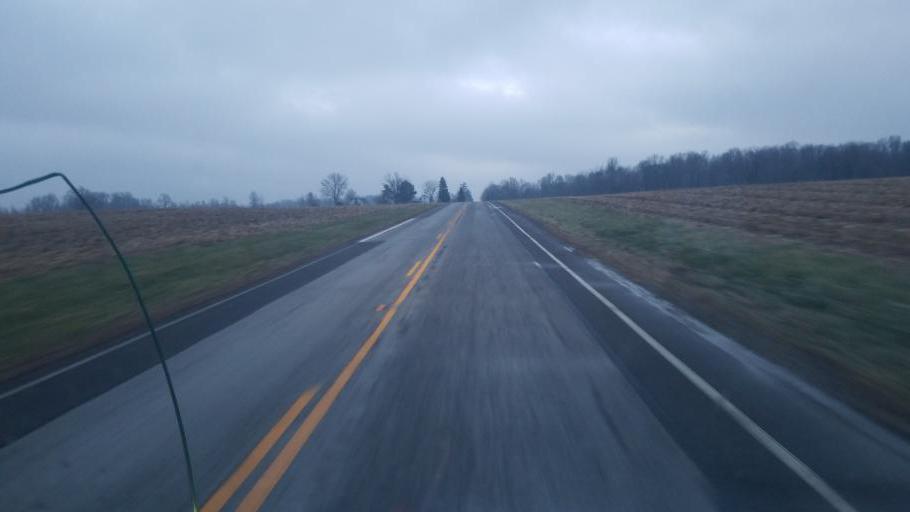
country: US
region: Ohio
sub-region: Wyandot County
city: Upper Sandusky
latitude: 40.8746
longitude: -83.1316
